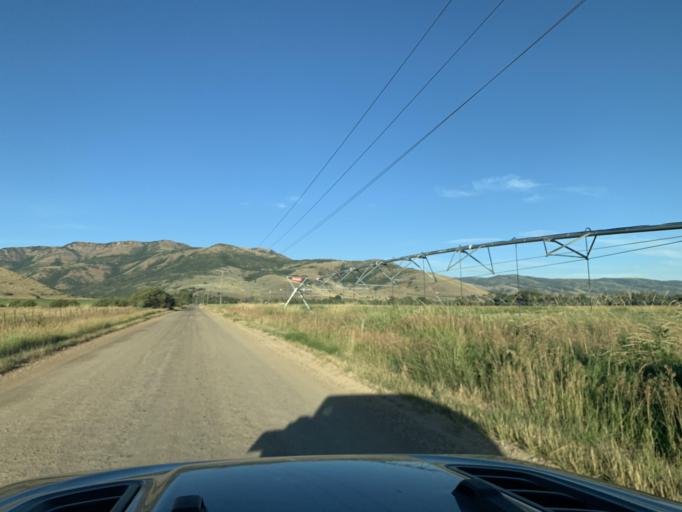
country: US
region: Utah
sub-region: Weber County
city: Wolf Creek
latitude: 41.2931
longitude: -111.7740
